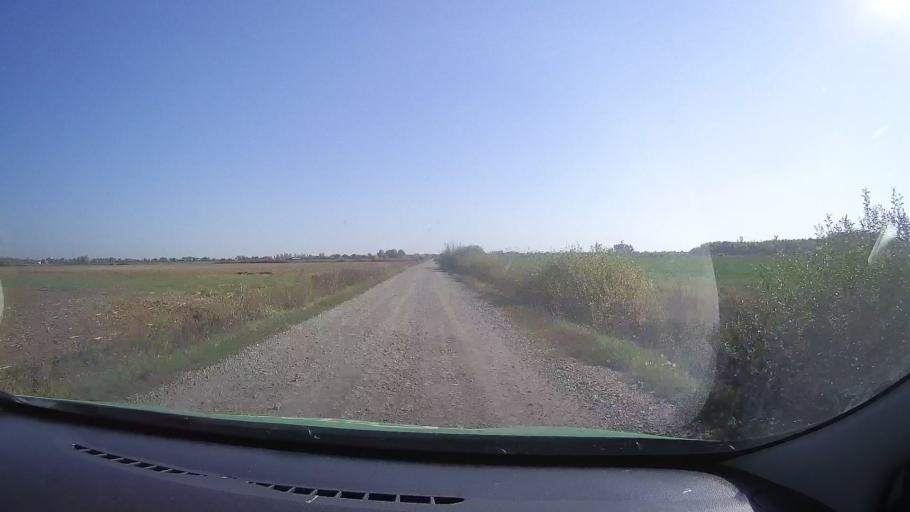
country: RO
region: Satu Mare
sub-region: Comuna Berveni
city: Berveni
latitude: 47.7343
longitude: 22.4624
